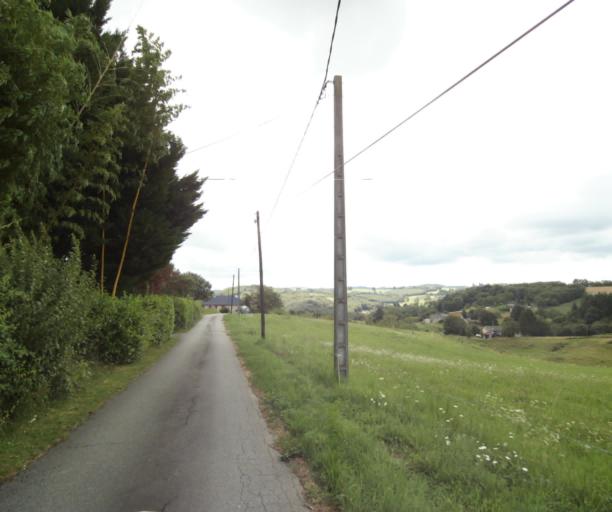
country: FR
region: Limousin
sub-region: Departement de la Correze
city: Sainte-Fortunade
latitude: 45.1755
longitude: 1.8360
